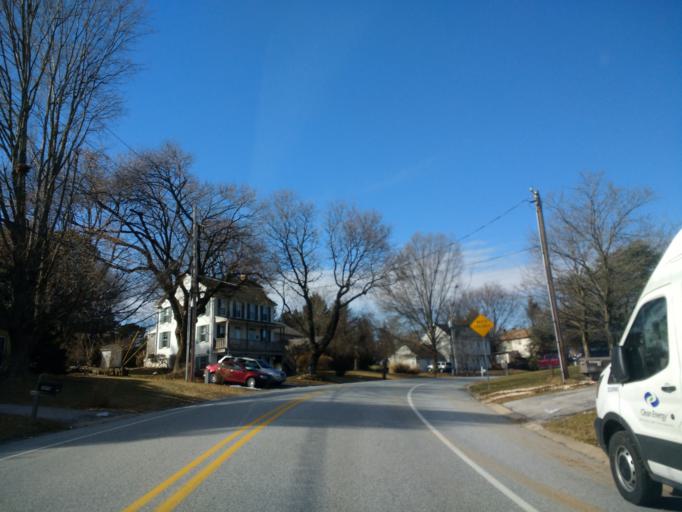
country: US
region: Pennsylvania
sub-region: York County
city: Spry
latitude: 39.9024
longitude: -76.6680
